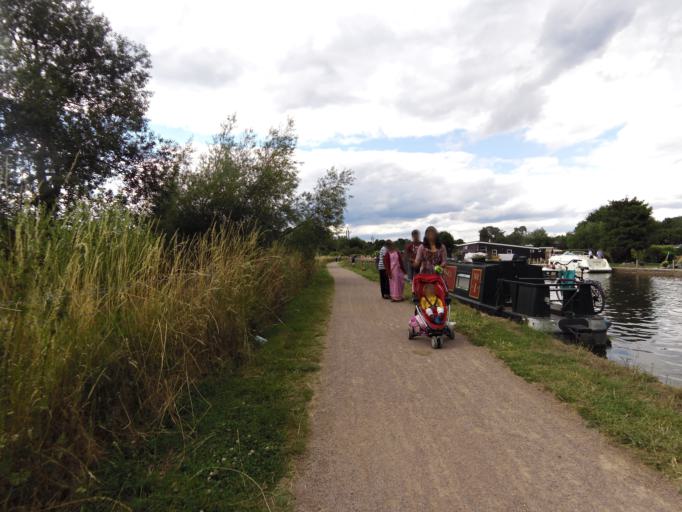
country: GB
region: England
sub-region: Hertfordshire
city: Broxbourne
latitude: 51.7400
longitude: -0.0135
